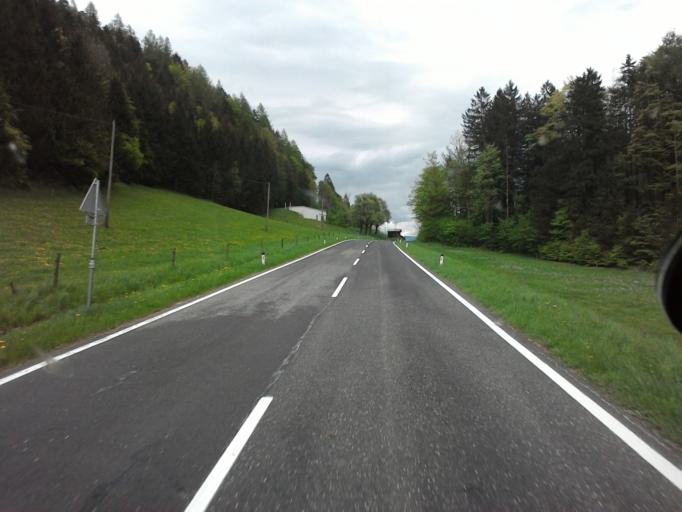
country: AT
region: Upper Austria
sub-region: Politischer Bezirk Kirchdorf an der Krems
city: Rossleithen
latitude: 47.7502
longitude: 14.2344
